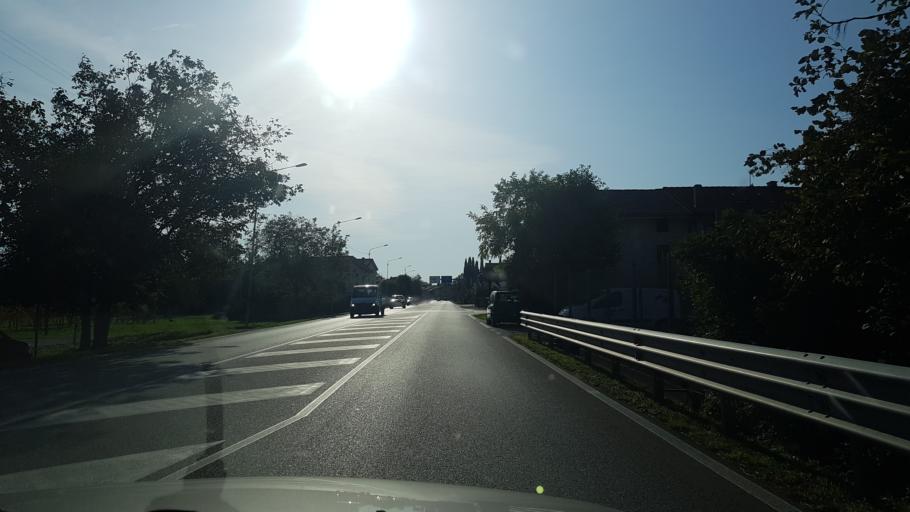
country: IT
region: Friuli Venezia Giulia
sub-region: Provincia di Udine
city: Gemona
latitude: 46.2547
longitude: 13.1132
